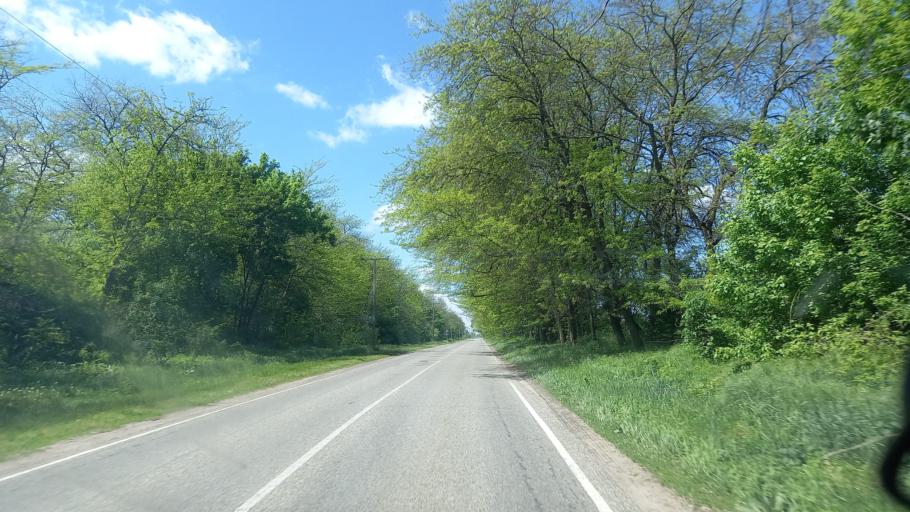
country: RU
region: Krasnodarskiy
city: Tbilisskaya
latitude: 45.3391
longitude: 40.3176
